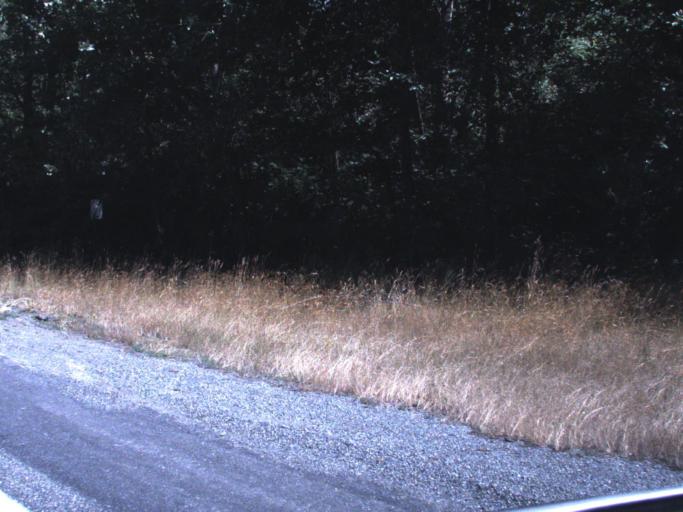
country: US
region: Washington
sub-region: King County
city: Enumclaw
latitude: 47.1930
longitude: -121.9356
